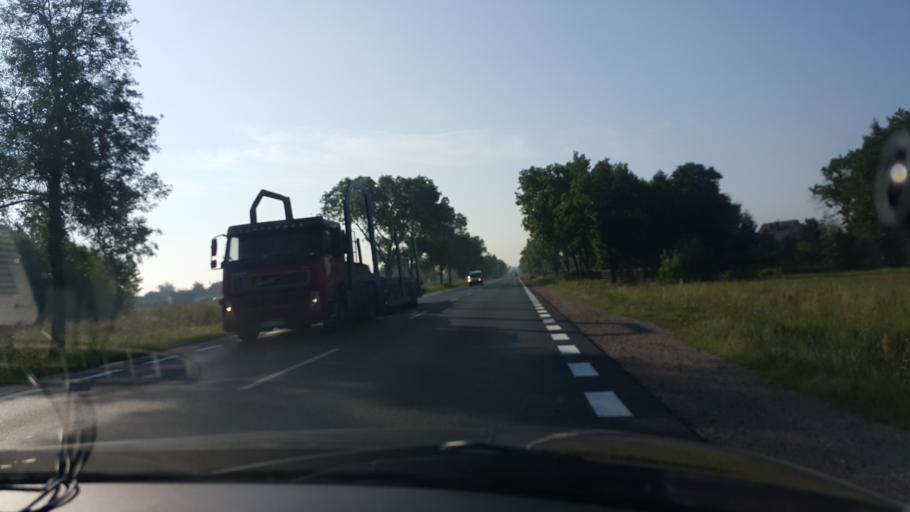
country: PL
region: Masovian Voivodeship
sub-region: Powiat radomski
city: Jedlnia-Letnisko
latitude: 51.3954
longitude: 21.2651
